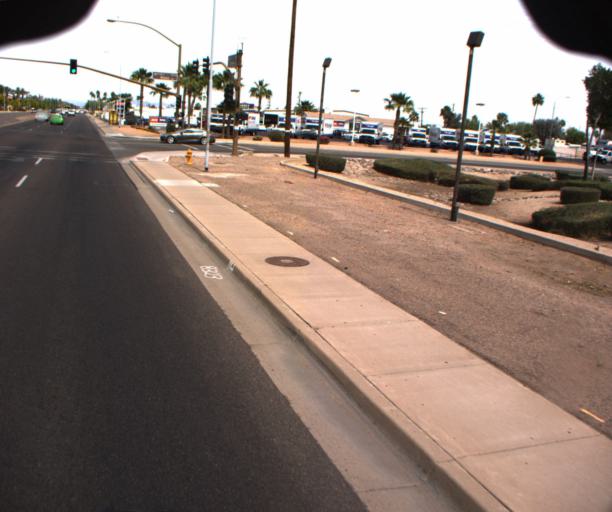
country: US
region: Arizona
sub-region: Maricopa County
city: San Carlos
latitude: 33.3274
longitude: -111.8416
